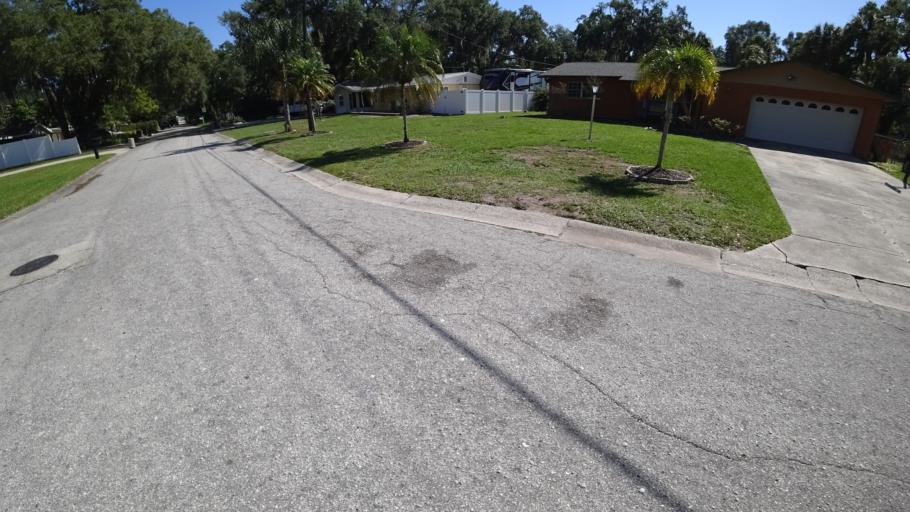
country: US
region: Florida
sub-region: Manatee County
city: West Bradenton
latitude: 27.4752
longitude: -82.6094
